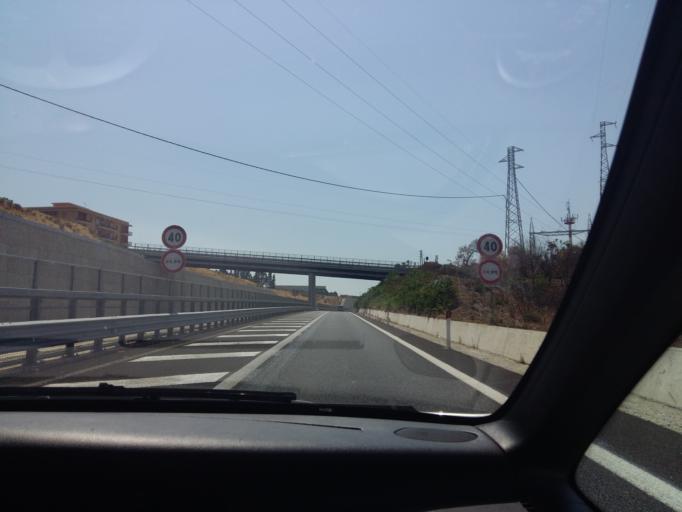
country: IT
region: Calabria
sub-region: Provincia di Reggio Calabria
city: Campo Calabro
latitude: 38.2192
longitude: 15.6477
